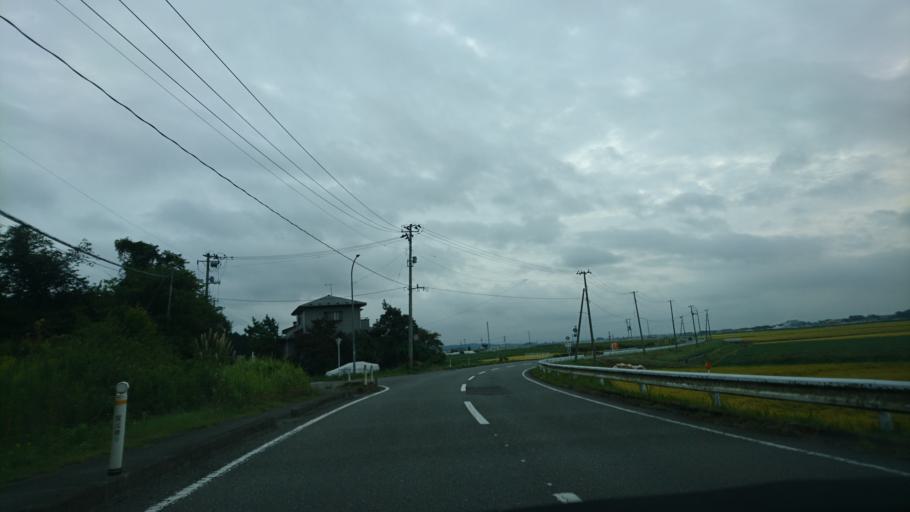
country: JP
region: Iwate
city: Ichinoseki
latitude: 38.8058
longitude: 141.1115
